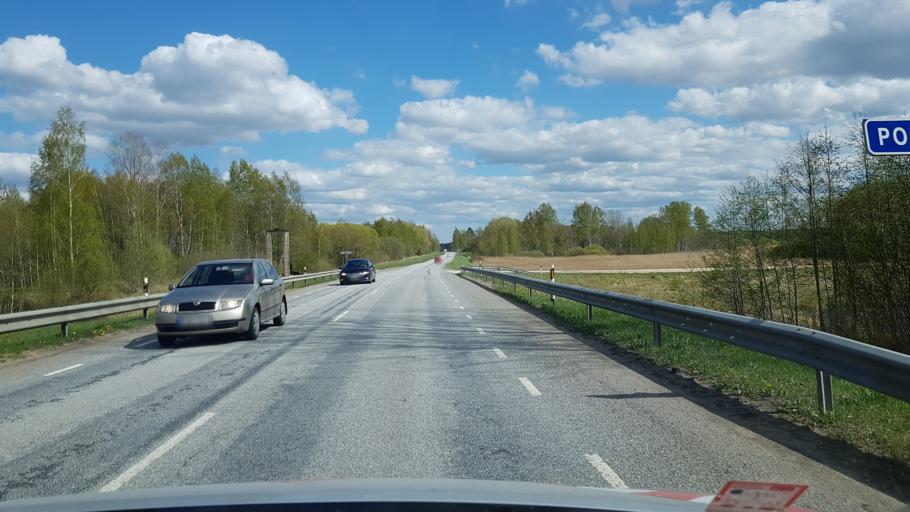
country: EE
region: Tartu
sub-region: UElenurme vald
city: Ulenurme
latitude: 58.3302
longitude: 26.7326
